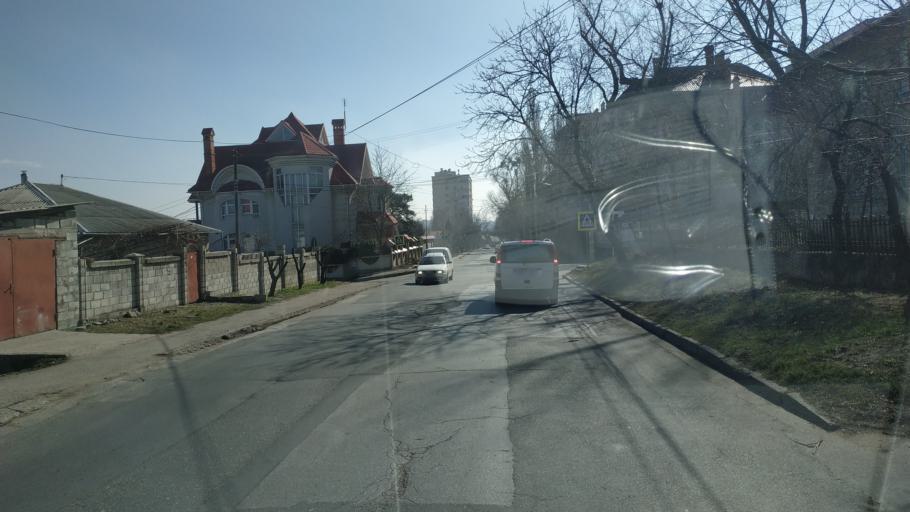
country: MD
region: Chisinau
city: Chisinau
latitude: 47.0326
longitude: 28.7987
